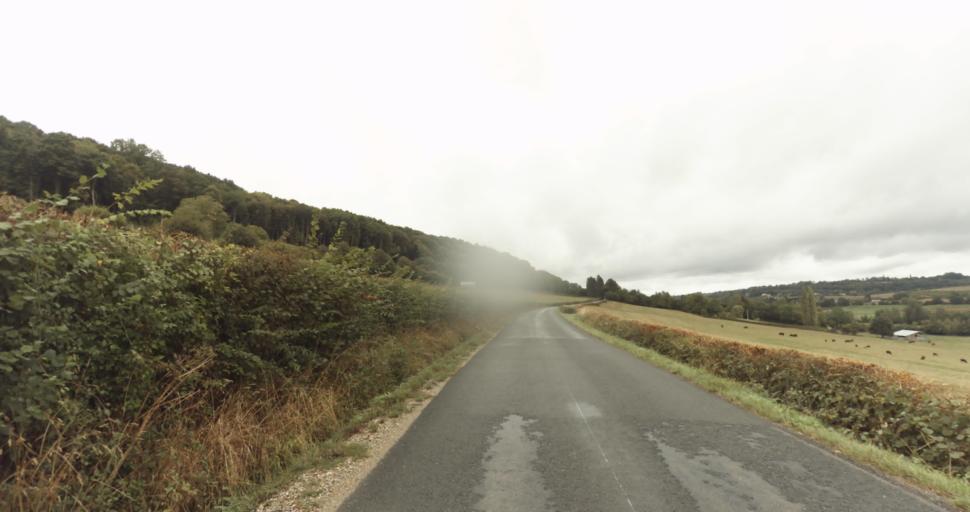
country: FR
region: Lower Normandy
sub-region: Departement de l'Orne
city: Vimoutiers
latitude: 48.8989
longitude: 0.2087
